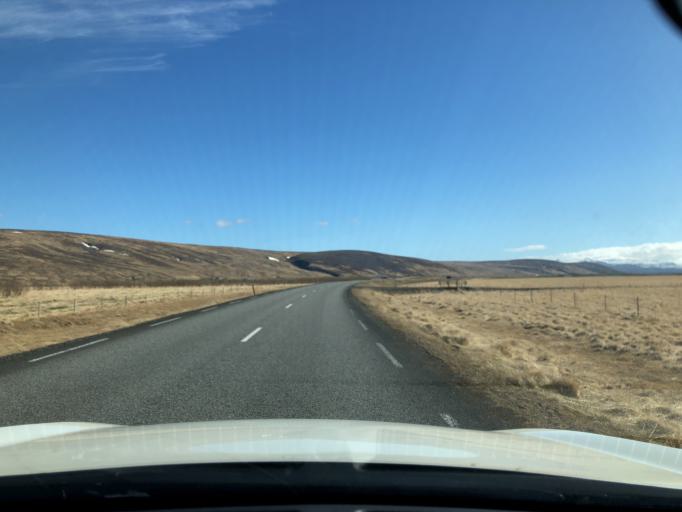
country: IS
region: South
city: Hveragerdi
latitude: 64.6974
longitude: -21.2348
